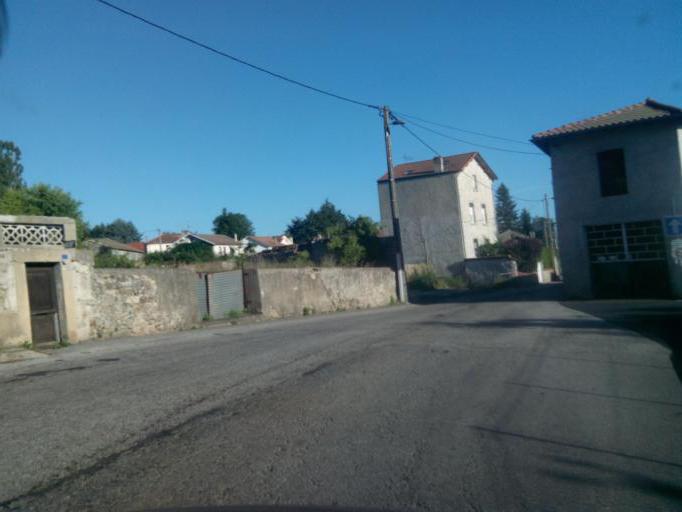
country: FR
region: Auvergne
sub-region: Departement de la Haute-Loire
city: Craponne-sur-Arzon
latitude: 45.3302
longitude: 3.8484
